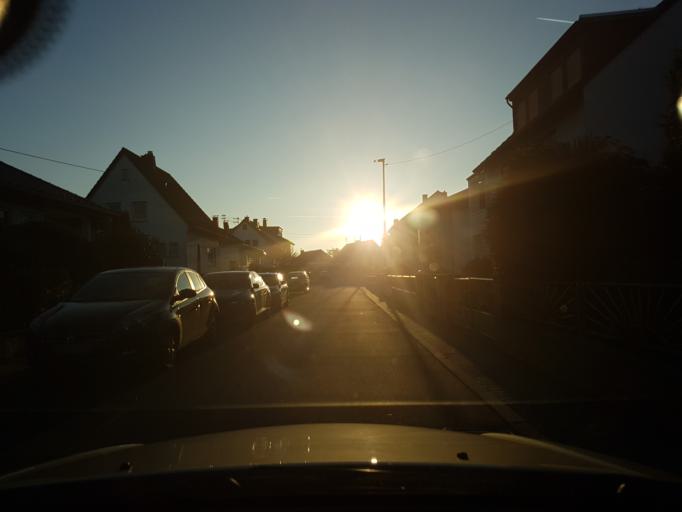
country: DE
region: Hesse
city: Taunusstein
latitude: 50.1515
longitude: 8.1849
